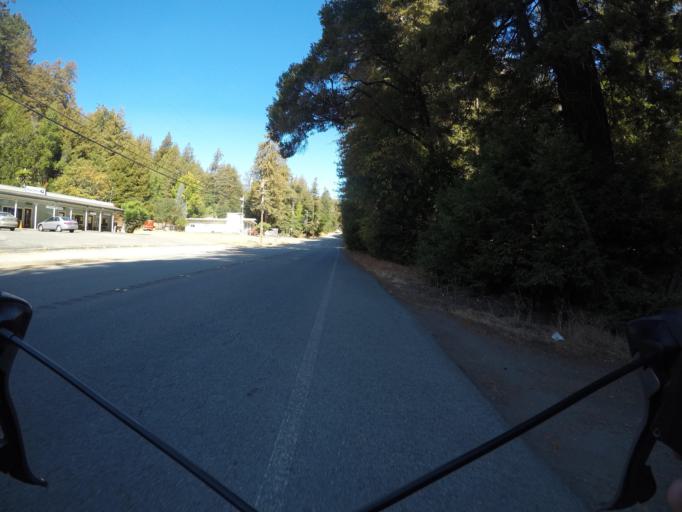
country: US
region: California
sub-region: San Mateo County
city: Portola Valley
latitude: 37.3199
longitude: -122.2743
